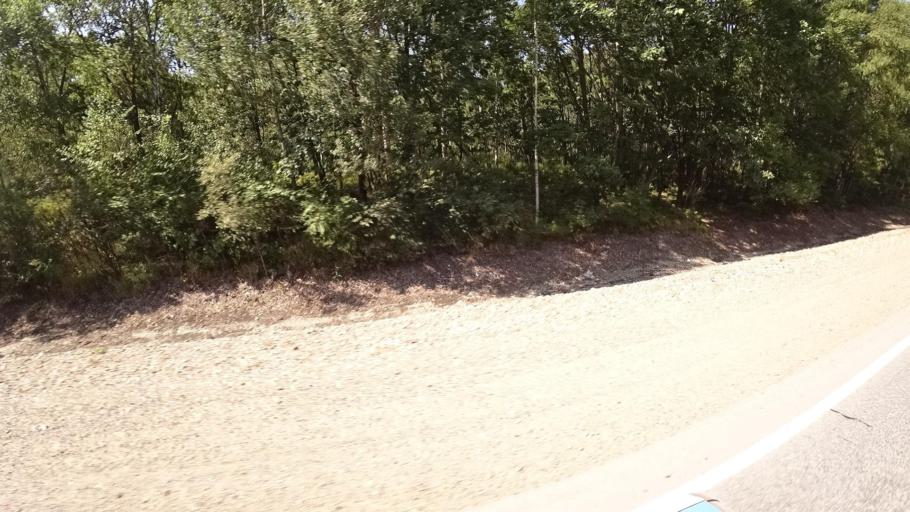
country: RU
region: Khabarovsk Krai
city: Khor
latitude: 47.9844
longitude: 135.0887
